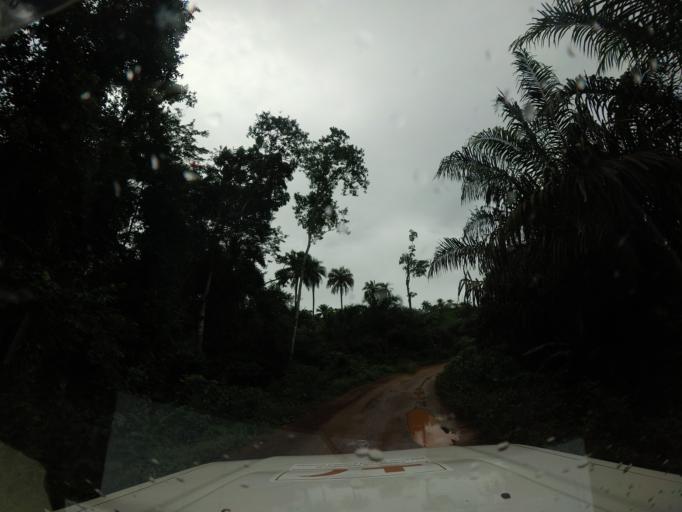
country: SL
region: Eastern Province
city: Kenema
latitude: 7.7136
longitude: -11.1852
